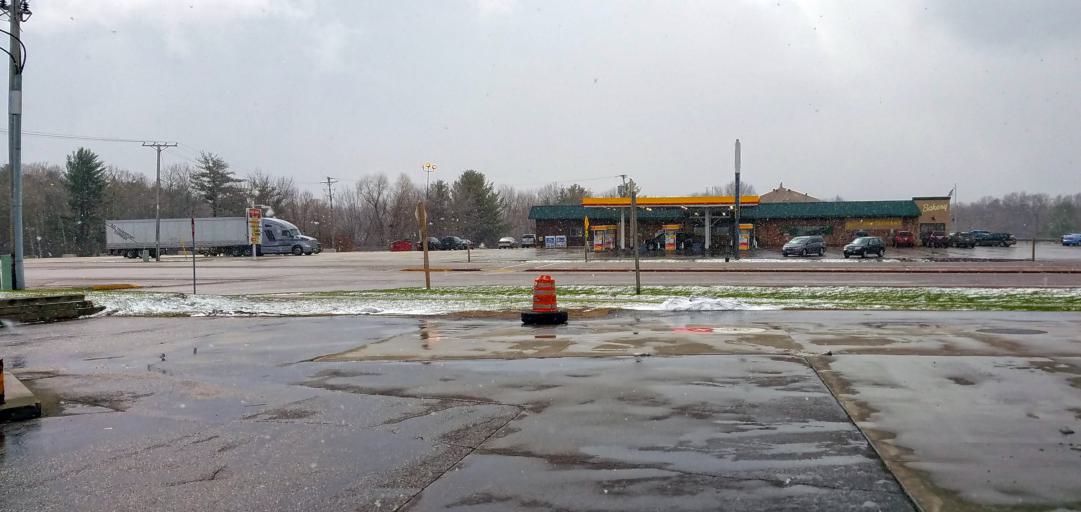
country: US
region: Wisconsin
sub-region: Juneau County
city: Mauston
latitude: 43.7967
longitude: -90.0522
